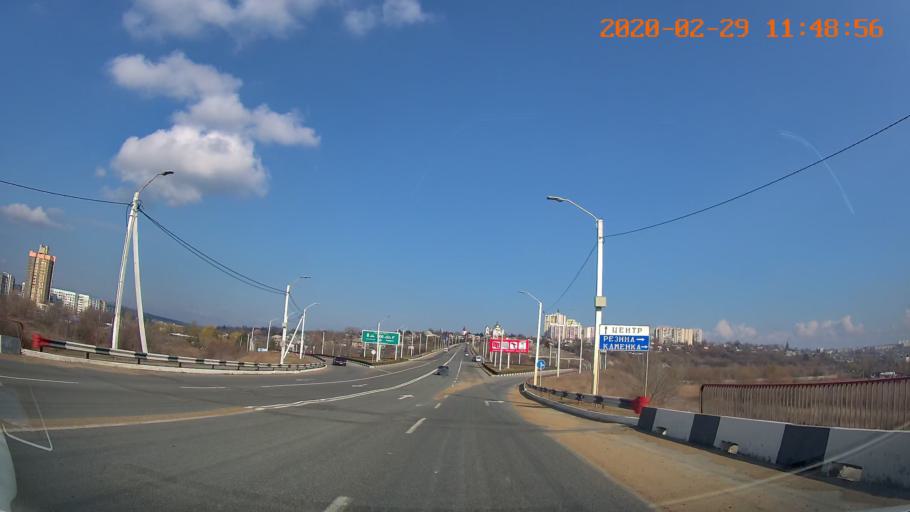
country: MD
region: Telenesti
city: Ribnita
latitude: 47.7514
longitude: 28.9931
